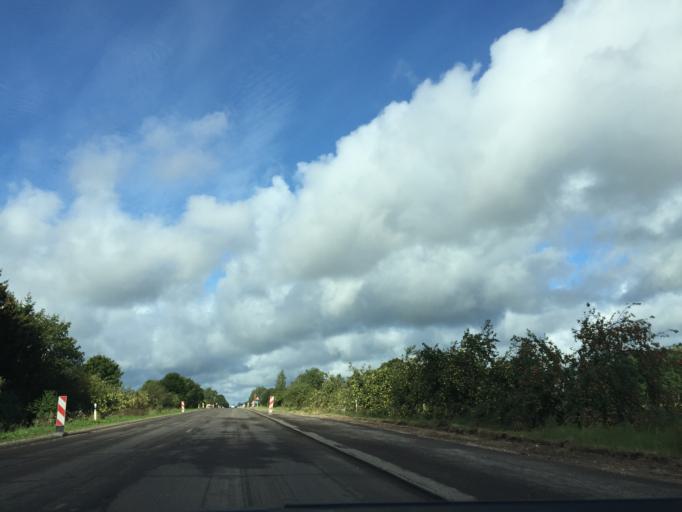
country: LV
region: Tukuma Rajons
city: Tukums
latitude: 56.9285
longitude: 23.2209
